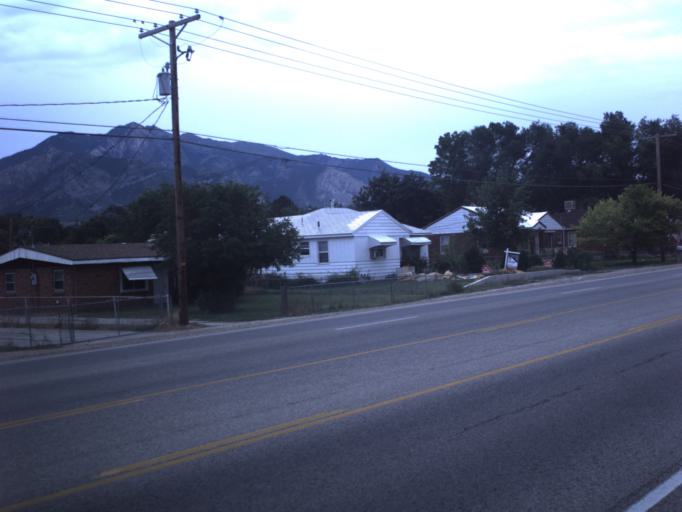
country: US
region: Utah
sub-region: Weber County
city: Harrisville
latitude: 41.2658
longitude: -111.9778
